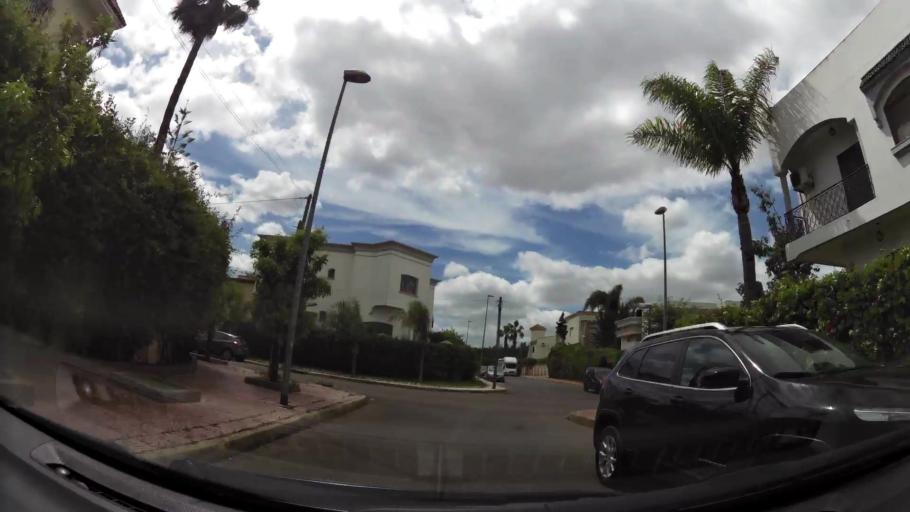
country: MA
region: Grand Casablanca
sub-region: Casablanca
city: Casablanca
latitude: 33.5601
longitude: -7.6226
